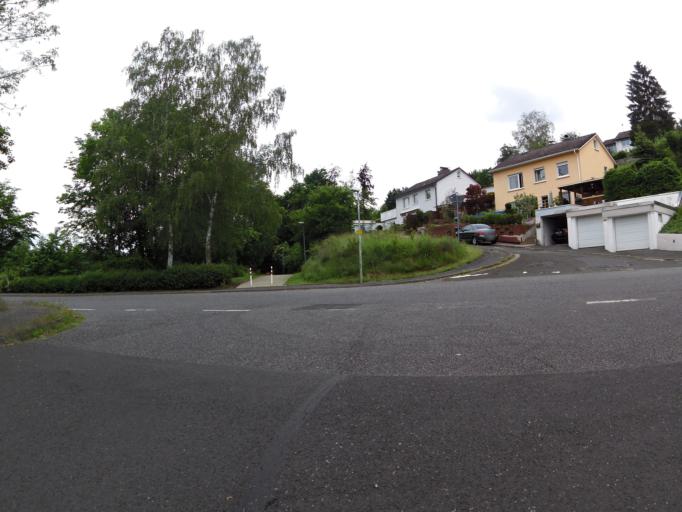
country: DE
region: Hesse
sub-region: Regierungsbezirk Kassel
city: Bad Hersfeld
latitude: 50.8704
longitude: 9.6839
